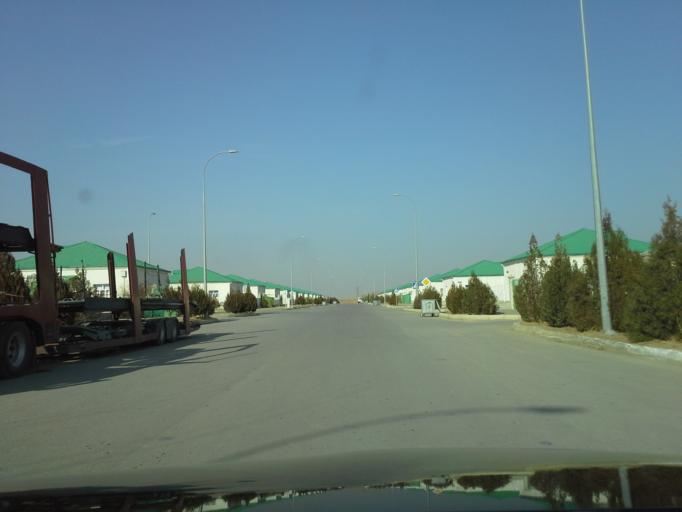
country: TM
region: Ahal
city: Abadan
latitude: 38.1697
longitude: 58.0528
